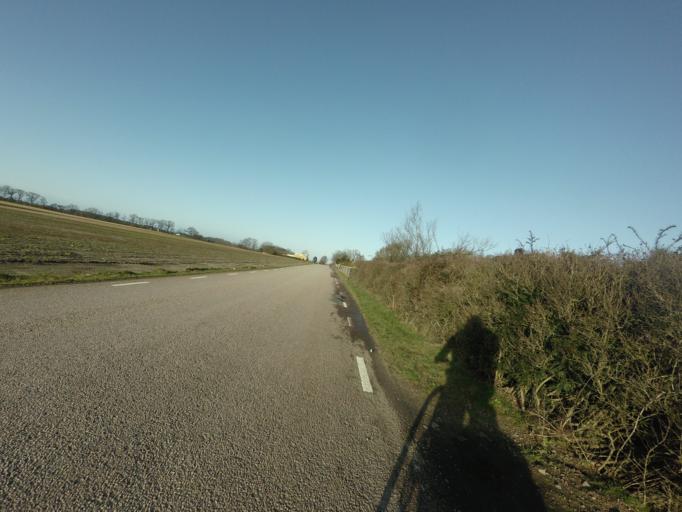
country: SE
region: Skane
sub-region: Helsingborg
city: Odakra
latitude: 56.1332
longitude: 12.6454
